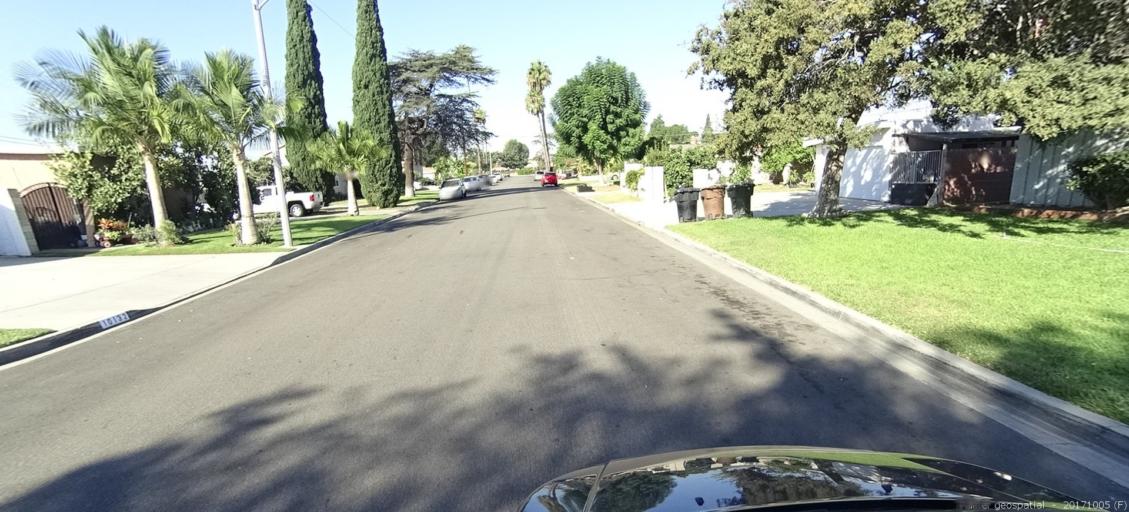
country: US
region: California
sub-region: Orange County
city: Garden Grove
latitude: 33.8018
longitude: -117.9561
